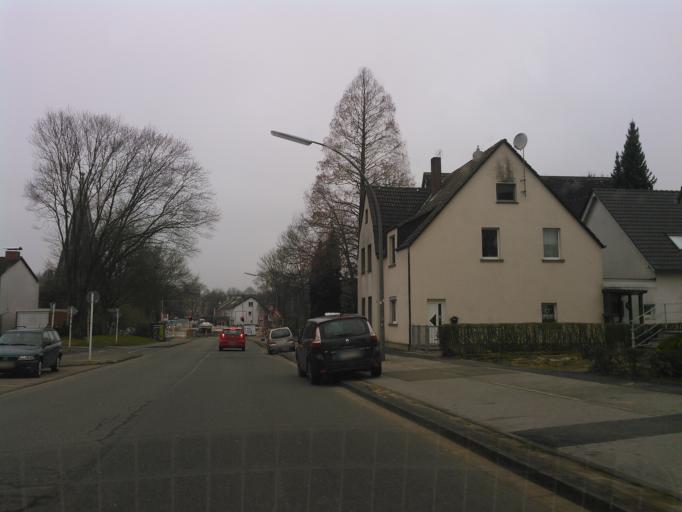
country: DE
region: North Rhine-Westphalia
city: Marl
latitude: 51.6531
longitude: 7.1177
